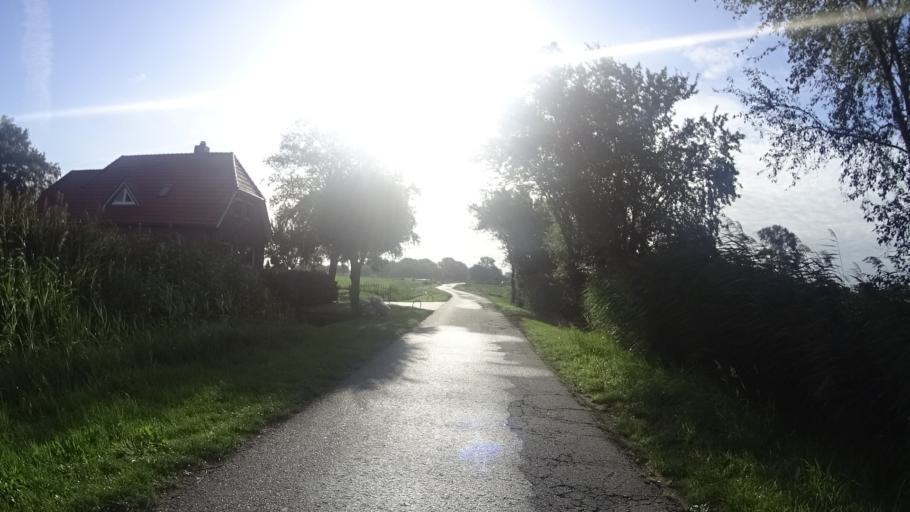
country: DE
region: Lower Saxony
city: Nordenham
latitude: 53.4958
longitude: 8.4375
